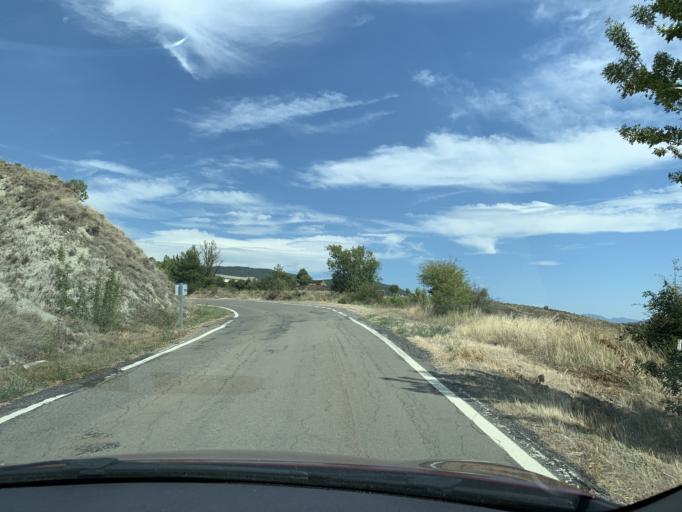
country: ES
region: Aragon
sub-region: Provincia de Huesca
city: Borau
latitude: 42.5931
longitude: -0.6329
